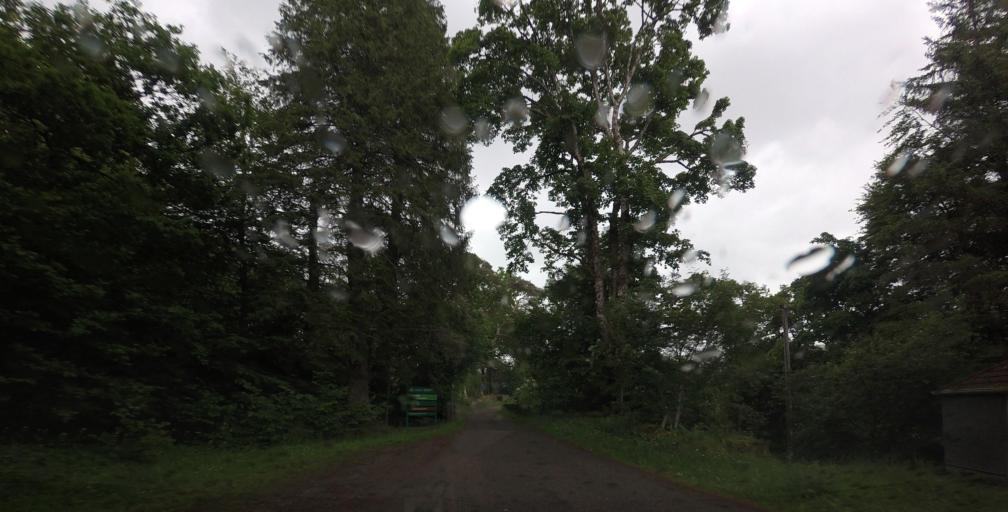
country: GB
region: Scotland
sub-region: Argyll and Bute
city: Oban
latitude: 56.7085
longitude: -5.5624
